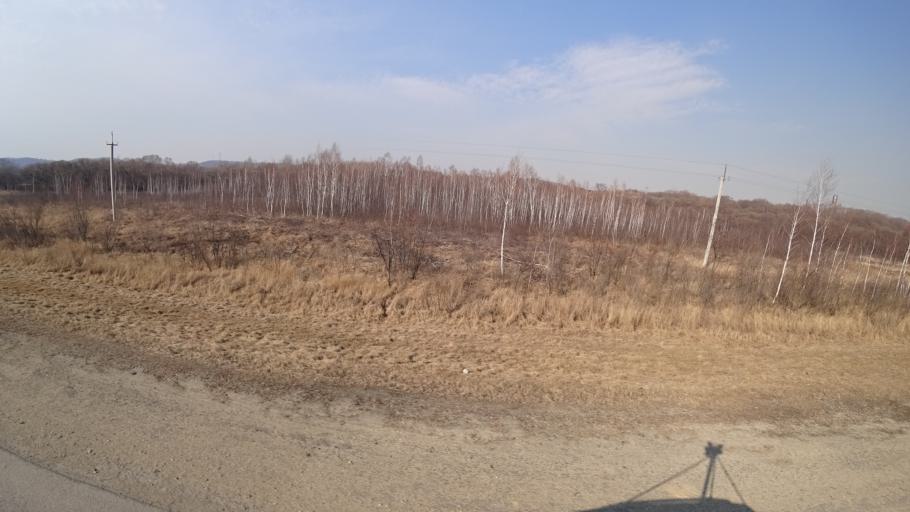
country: RU
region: Amur
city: Novobureyskiy
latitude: 49.7935
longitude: 129.9160
